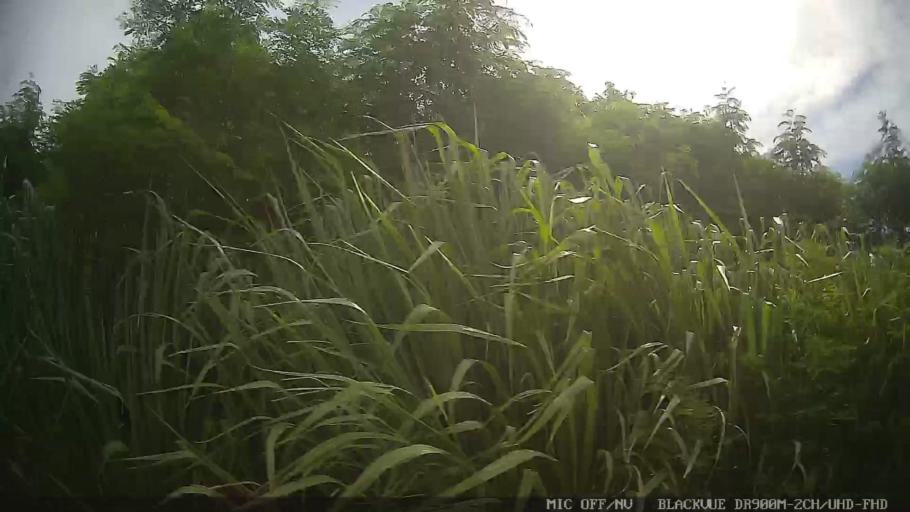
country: BR
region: Sao Paulo
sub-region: Conchas
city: Conchas
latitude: -23.0203
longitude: -47.9981
